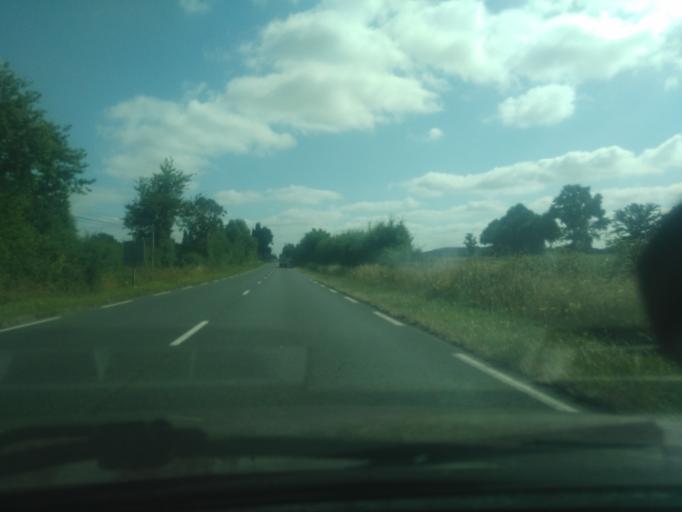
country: FR
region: Pays de la Loire
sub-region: Departement de la Vendee
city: La Ferriere
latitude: 46.7325
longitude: -1.2853
